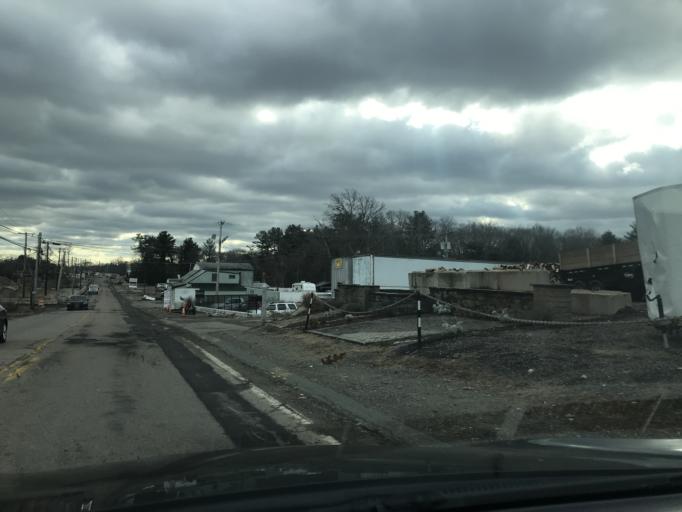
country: US
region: Massachusetts
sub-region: Plymouth County
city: Abington
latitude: 42.1417
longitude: -70.9527
